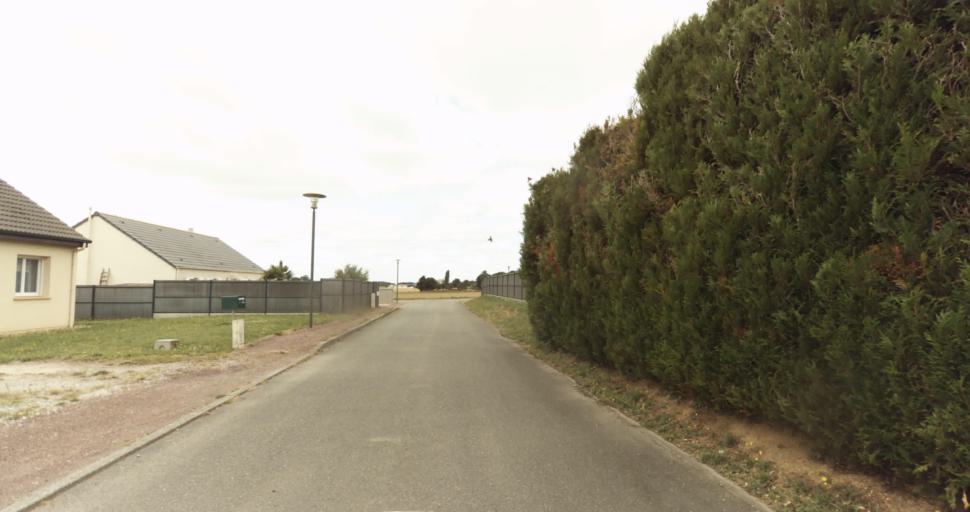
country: FR
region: Haute-Normandie
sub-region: Departement de l'Eure
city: Marcilly-sur-Eure
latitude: 48.9203
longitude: 1.2495
